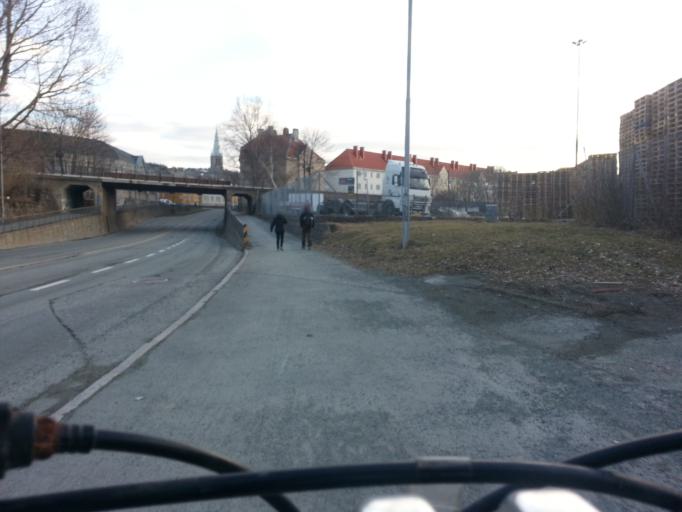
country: NO
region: Sor-Trondelag
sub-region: Trondheim
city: Trondheim
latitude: 63.4404
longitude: 10.4312
